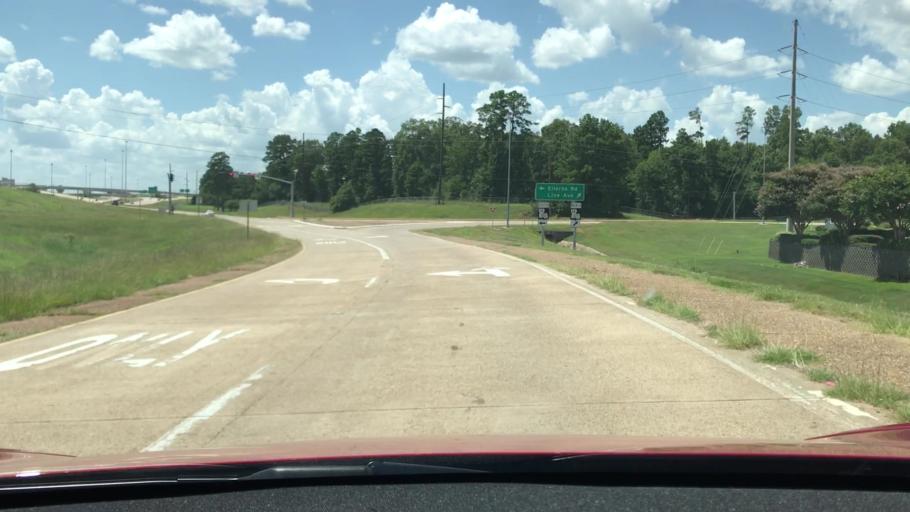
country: US
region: Louisiana
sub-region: Bossier Parish
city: Bossier City
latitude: 32.4162
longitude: -93.7359
